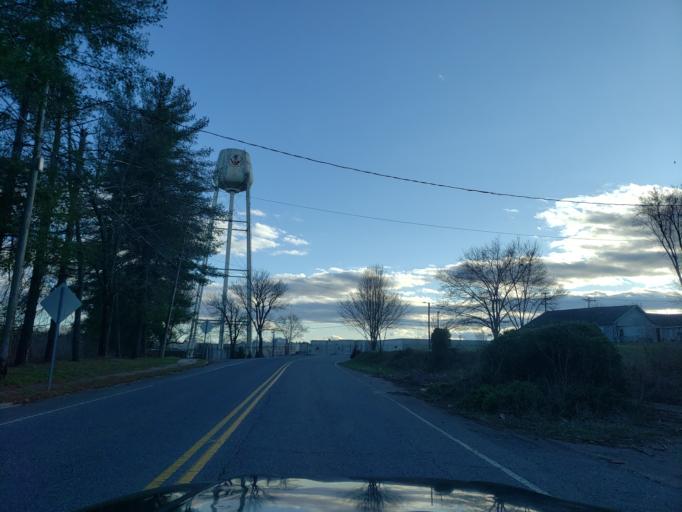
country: US
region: North Carolina
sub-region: Cleveland County
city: Shelby
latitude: 35.4146
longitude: -81.5611
